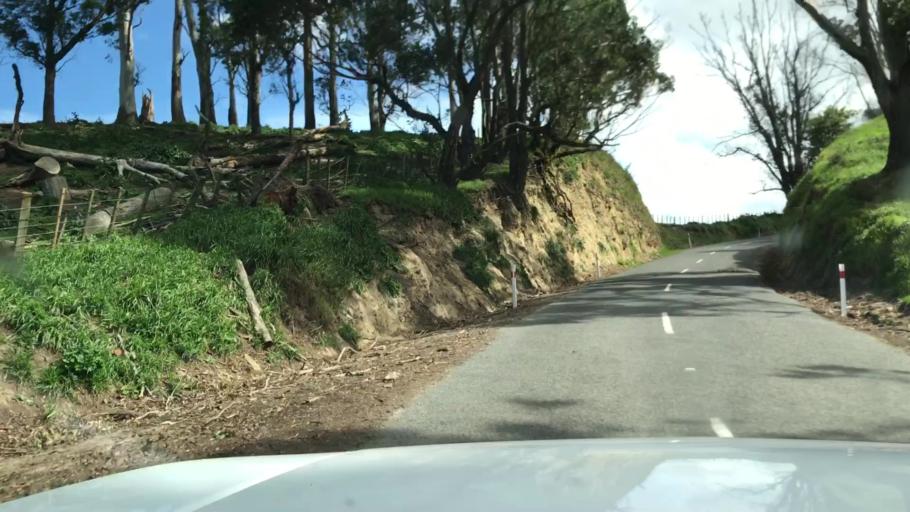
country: NZ
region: Hawke's Bay
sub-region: Hastings District
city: Hastings
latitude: -39.8152
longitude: 176.7511
